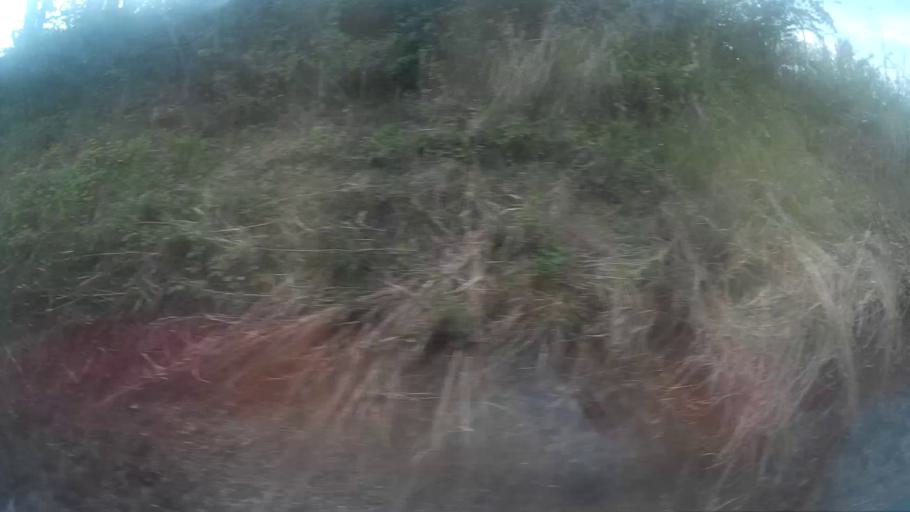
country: VN
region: Phu Yen
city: La Hai
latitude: 13.4330
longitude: 109.0747
